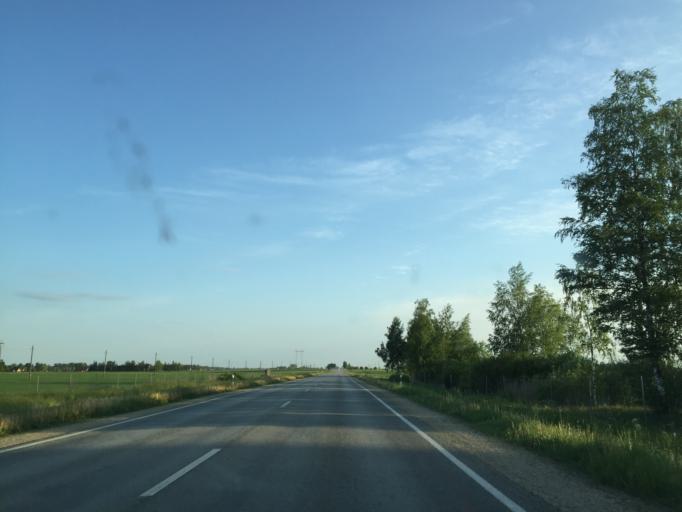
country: LT
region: Siauliu apskritis
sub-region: Joniskis
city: Joniskis
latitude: 56.1160
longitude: 23.4943
